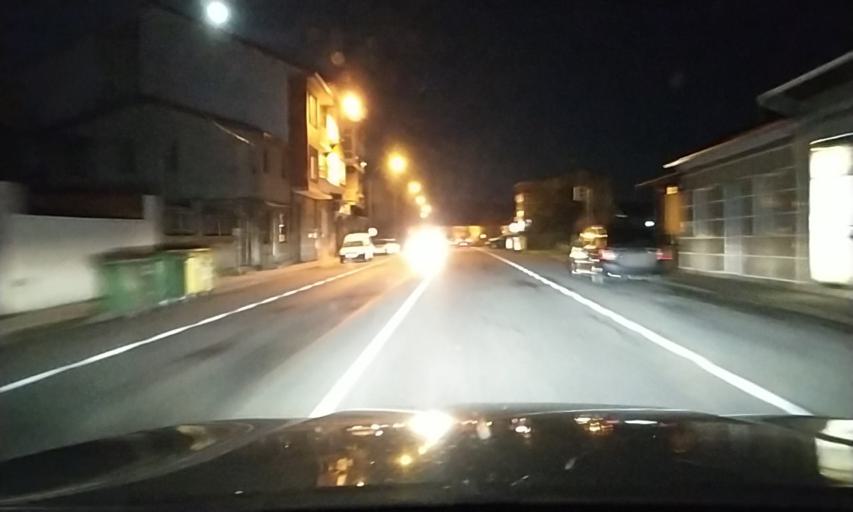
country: ES
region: Galicia
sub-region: Provincia de Ourense
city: Verin
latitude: 41.9388
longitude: -7.4514
